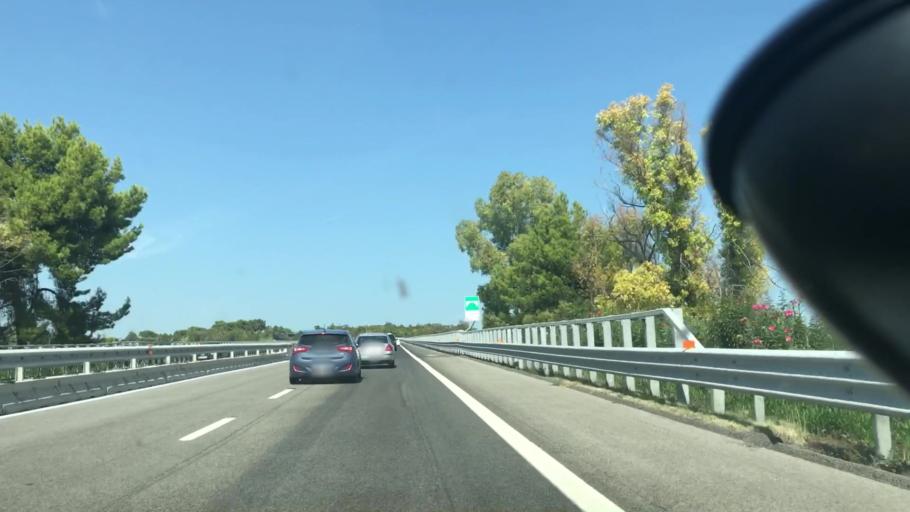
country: IT
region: Abruzzo
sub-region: Provincia di Chieti
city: Marina di Vasto
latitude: 42.0687
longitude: 14.7257
